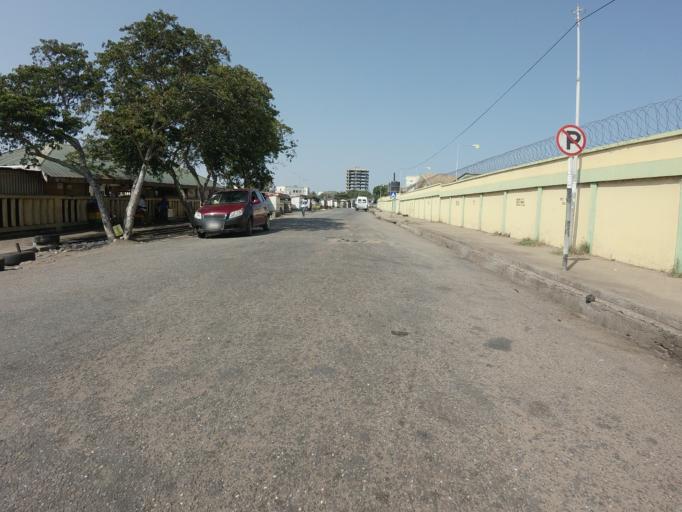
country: GH
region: Greater Accra
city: Accra
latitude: 5.5478
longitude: -0.2021
